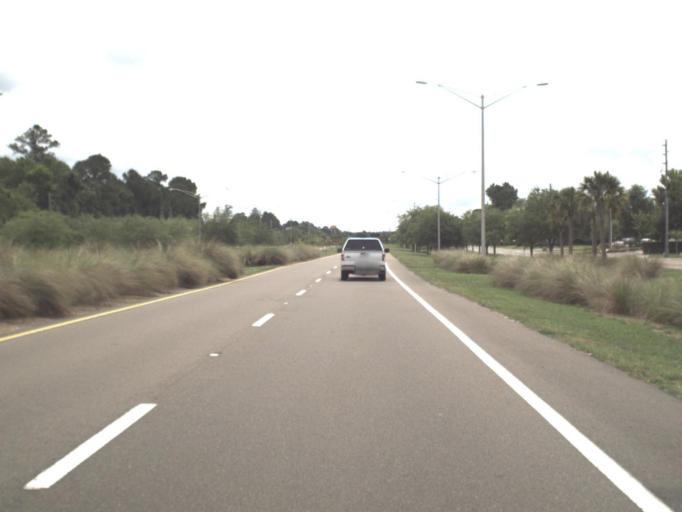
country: US
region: Florida
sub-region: Duval County
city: Jacksonville
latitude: 30.4835
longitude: -81.6569
